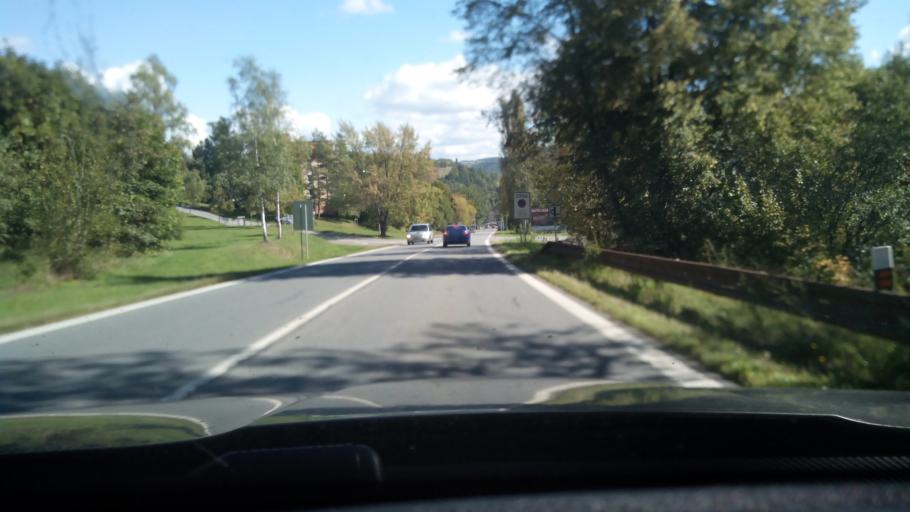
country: CZ
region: Jihocesky
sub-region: Okres Prachatice
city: Vimperk
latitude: 49.0603
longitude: 13.7723
